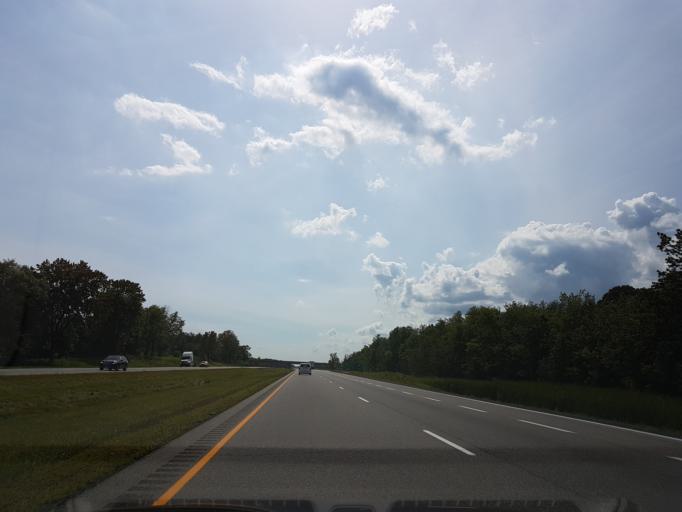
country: US
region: New York
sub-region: St. Lawrence County
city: Ogdensburg
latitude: 44.8140
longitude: -75.4003
